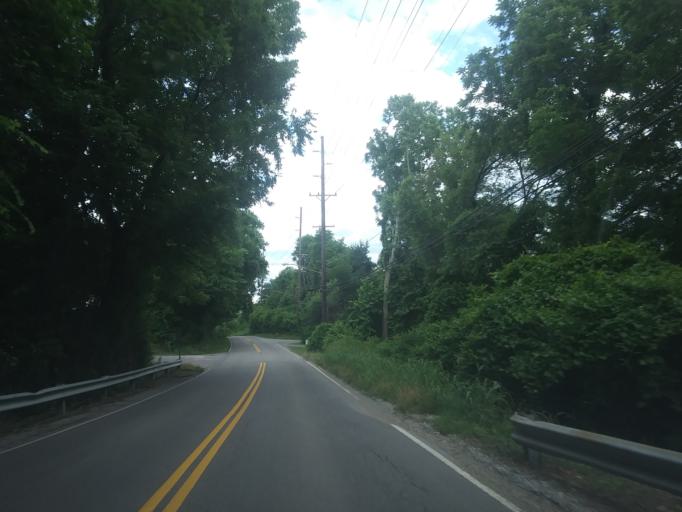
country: US
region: Tennessee
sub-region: Davidson County
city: Oak Hill
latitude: 36.0981
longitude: -86.7243
